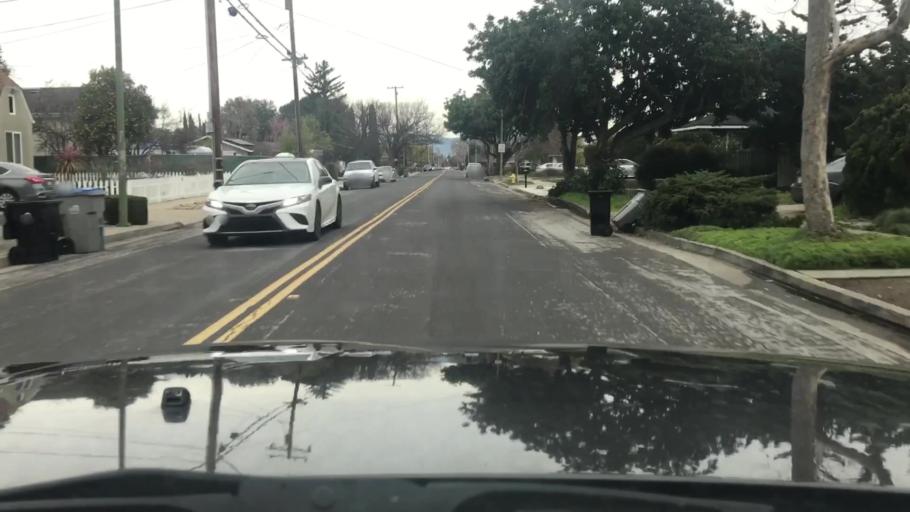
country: US
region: California
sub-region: Santa Clara County
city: Saratoga
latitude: 37.2833
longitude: -121.9920
